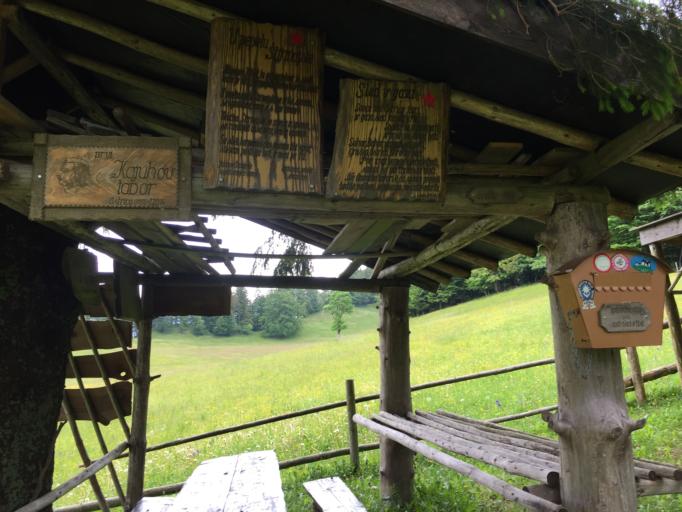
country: SI
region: Dobrna
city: Dobrna
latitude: 46.3873
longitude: 15.2201
